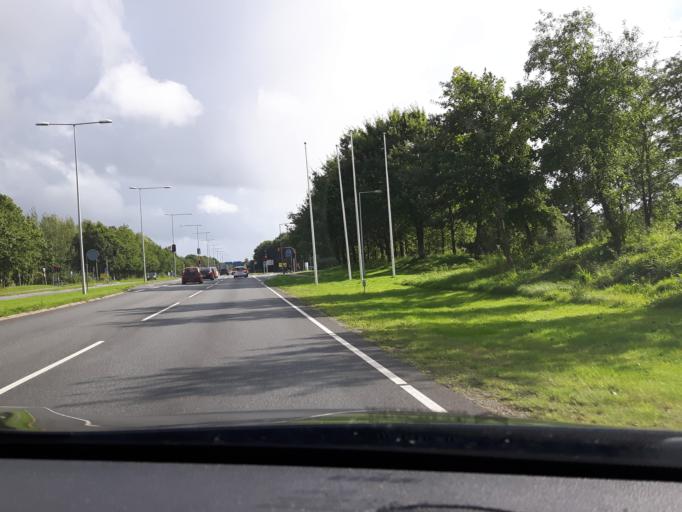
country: DK
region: Central Jutland
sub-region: Herning Kommune
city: Herning
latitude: 56.1461
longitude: 8.9383
